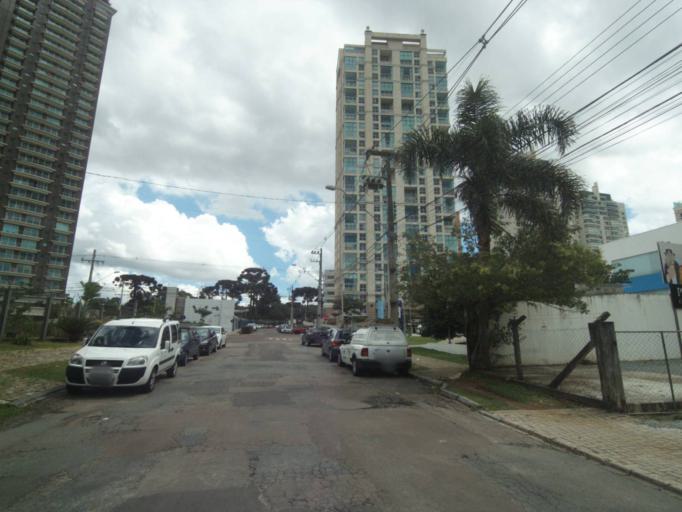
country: BR
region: Parana
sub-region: Curitiba
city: Curitiba
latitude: -25.4388
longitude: -49.3430
